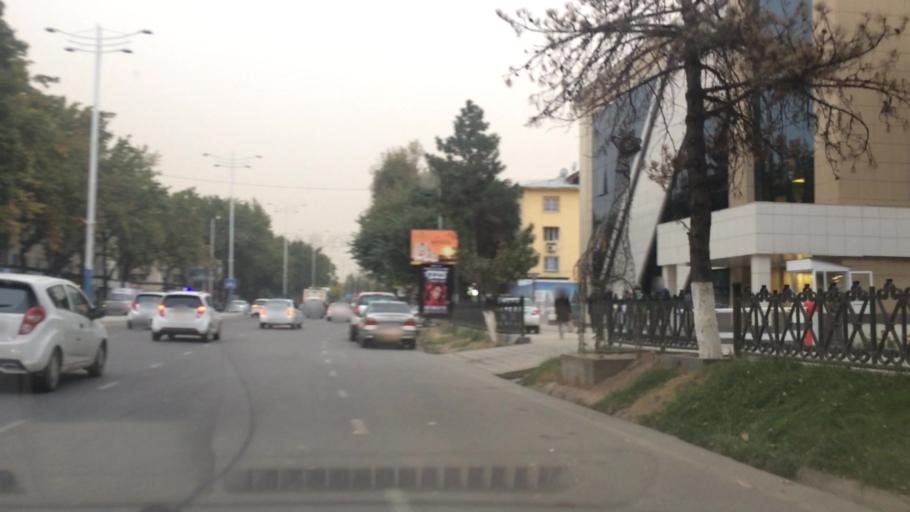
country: UZ
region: Toshkent Shahri
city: Tashkent
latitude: 41.2974
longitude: 69.2499
